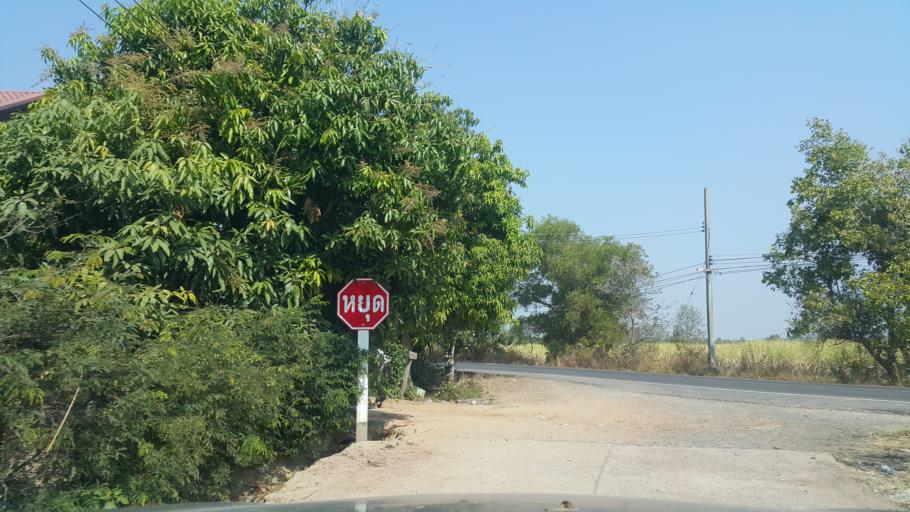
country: TH
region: Buriram
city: Satuek
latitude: 15.1144
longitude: 103.3790
